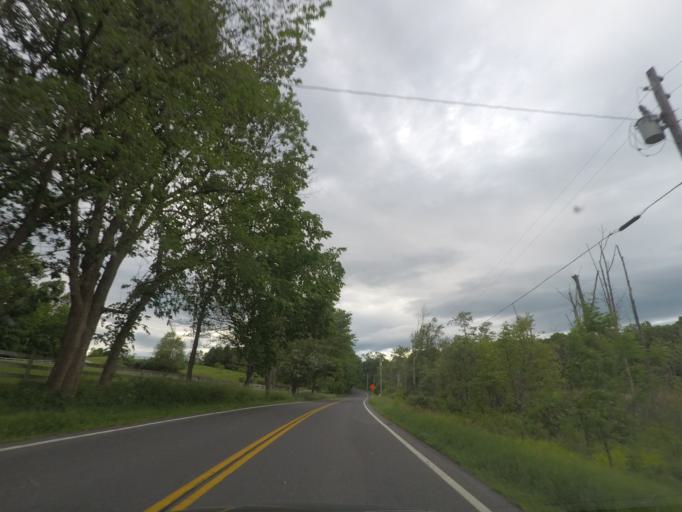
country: US
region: New York
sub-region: Dutchess County
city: Pine Plains
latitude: 41.9640
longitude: -73.5524
